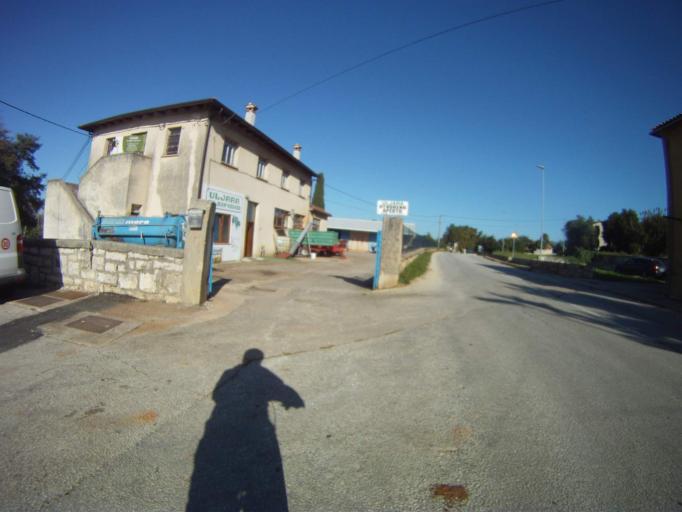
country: HR
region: Istarska
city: Buje
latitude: 45.3781
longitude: 13.6222
